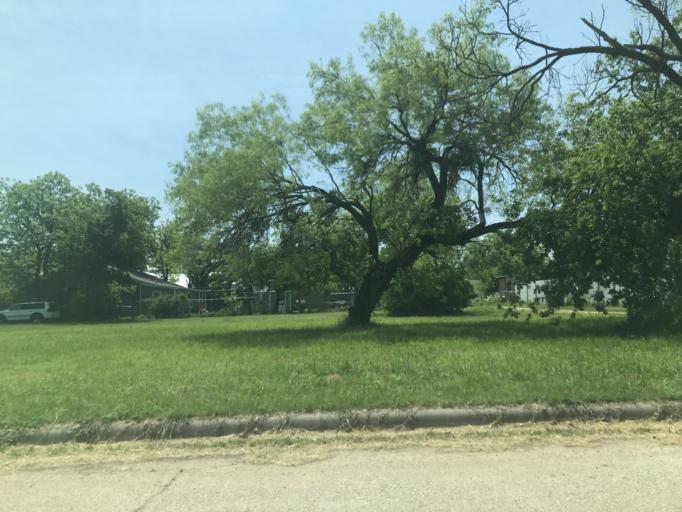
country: US
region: Texas
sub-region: Taylor County
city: Abilene
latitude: 32.4474
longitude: -99.7609
